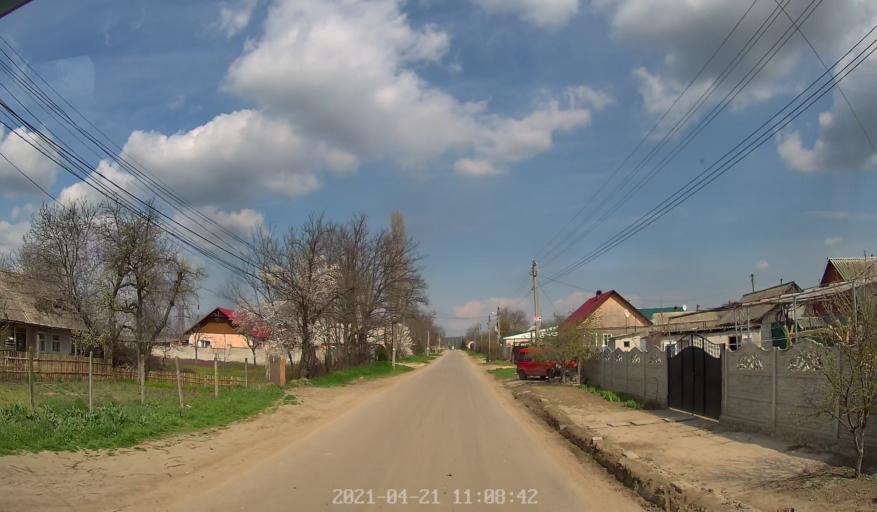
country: MD
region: Chisinau
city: Singera
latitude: 46.9561
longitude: 28.9412
